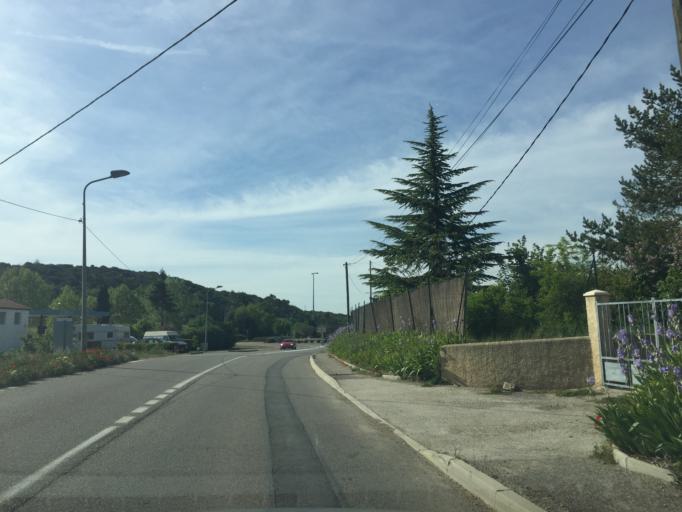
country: FR
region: Provence-Alpes-Cote d'Azur
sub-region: Departement du Var
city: Ginasservis
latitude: 43.6735
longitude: 5.8486
